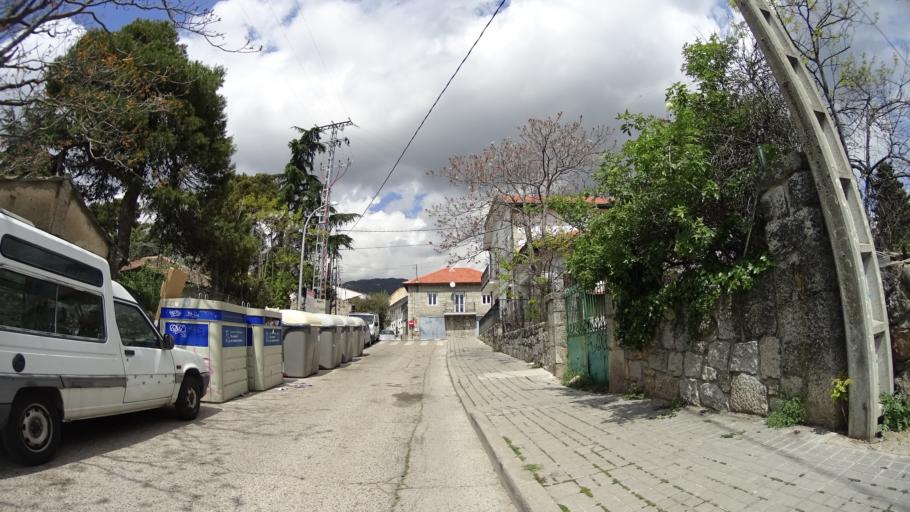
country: ES
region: Madrid
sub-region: Provincia de Madrid
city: Hoyo de Manzanares
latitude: 40.6212
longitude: -3.9046
